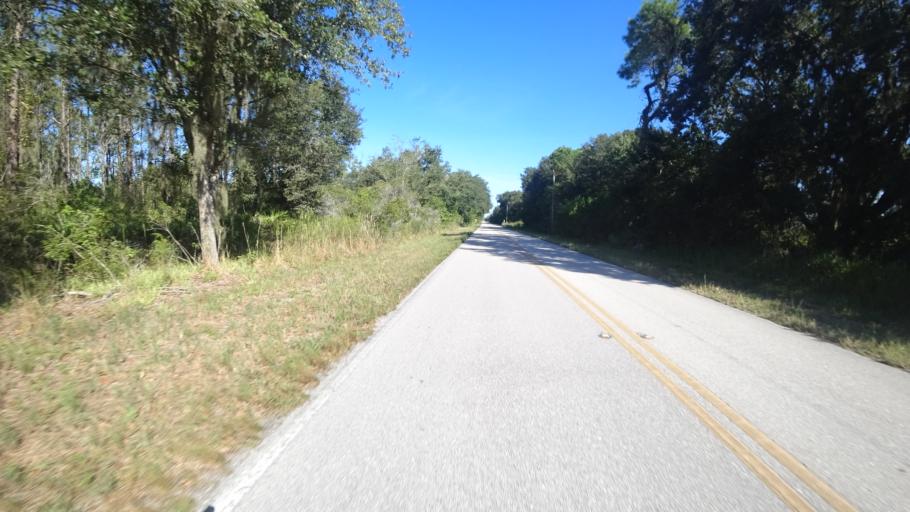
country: US
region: Florida
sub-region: Hillsborough County
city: Wimauma
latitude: 27.6258
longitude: -82.2925
